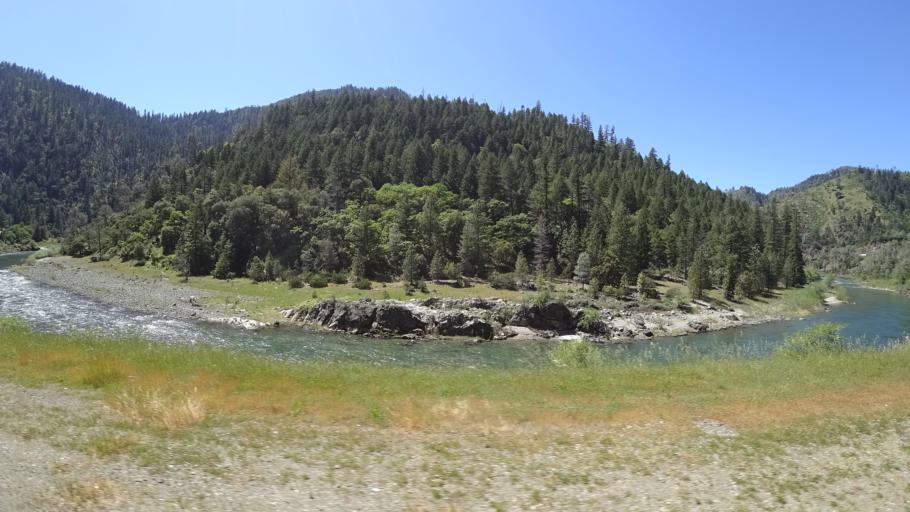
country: US
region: California
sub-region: Trinity County
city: Hayfork
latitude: 40.7890
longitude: -123.3479
